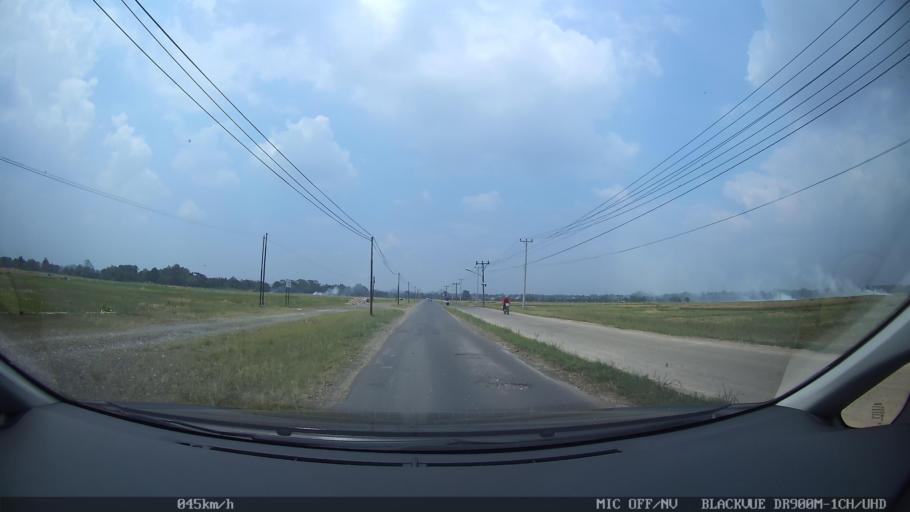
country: ID
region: Lampung
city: Pringsewu
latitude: -5.3583
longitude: 105.0092
